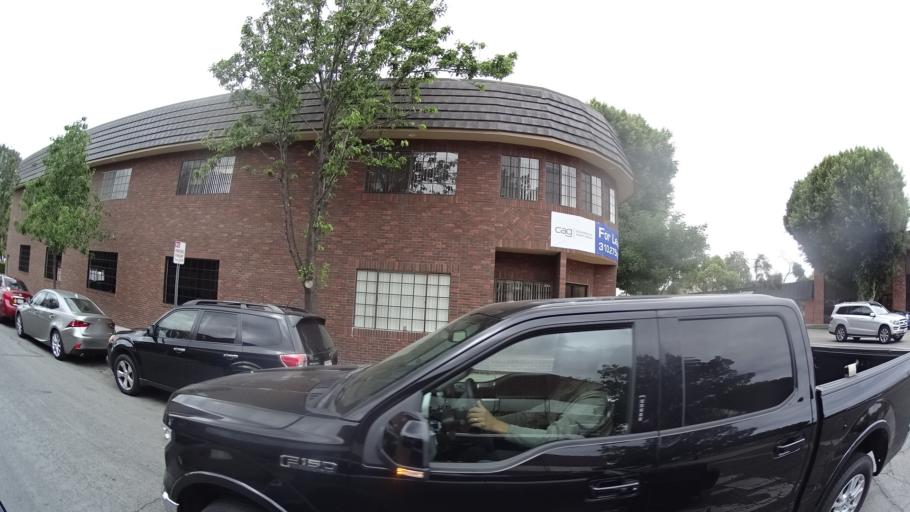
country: US
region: California
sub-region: Los Angeles County
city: Burbank
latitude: 34.1735
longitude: -118.3295
